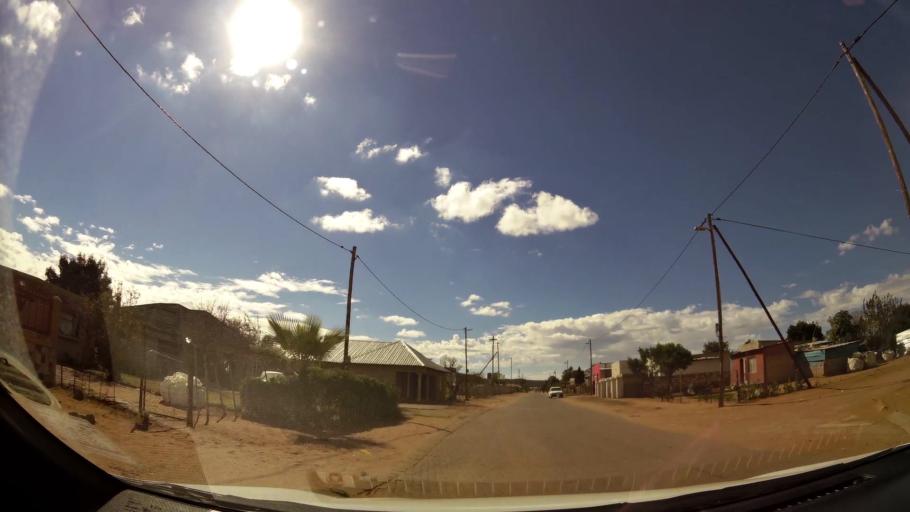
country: ZA
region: Limpopo
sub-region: Waterberg District Municipality
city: Bela-Bela
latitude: -24.8777
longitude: 28.3232
